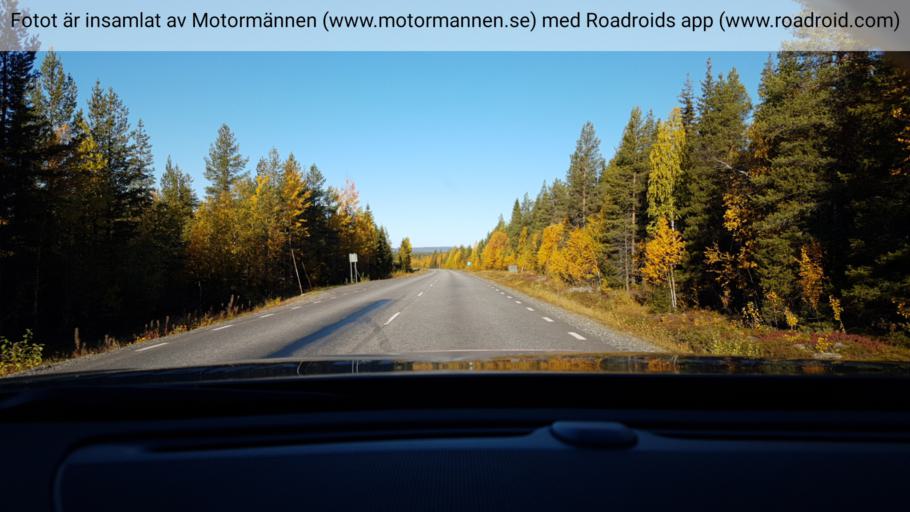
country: SE
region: Vaesterbotten
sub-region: Skelleftea Kommun
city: Storvik
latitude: 65.3695
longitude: 20.4000
